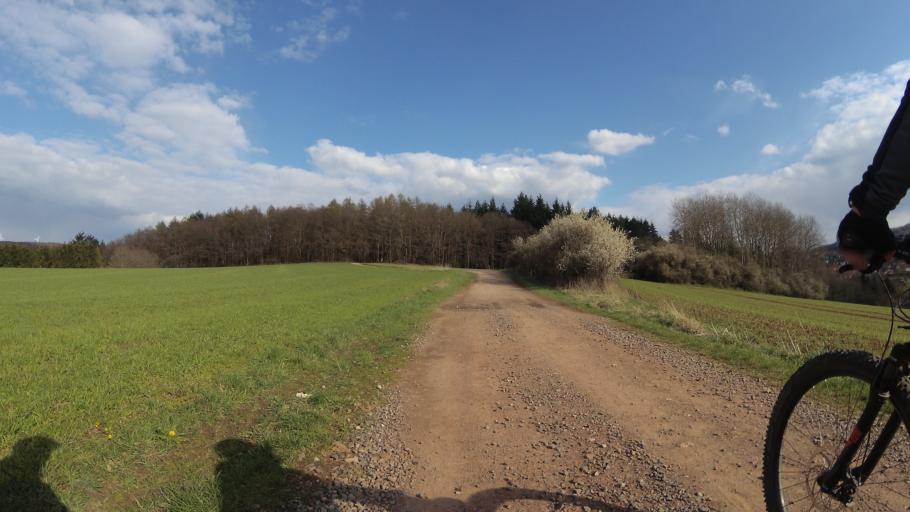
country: DE
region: Saarland
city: Tholey
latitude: 49.5098
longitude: 7.0293
